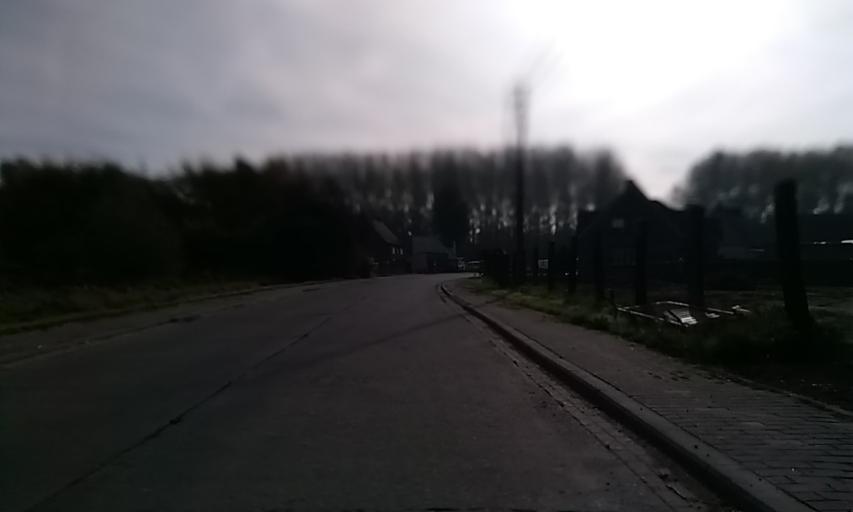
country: BE
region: Flanders
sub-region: Provincie Oost-Vlaanderen
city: Sint-Lievens-Houtem
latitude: 50.9280
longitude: 3.8327
